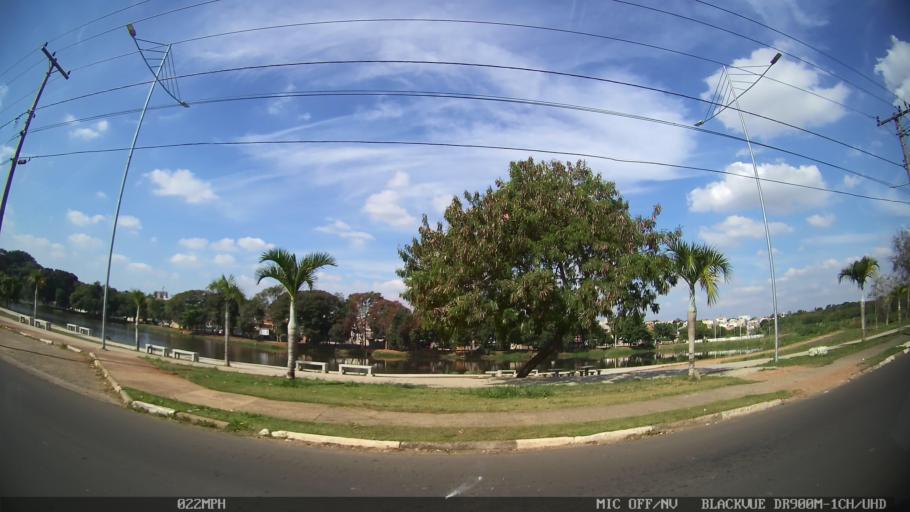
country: BR
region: Sao Paulo
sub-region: Hortolandia
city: Hortolandia
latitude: -22.8923
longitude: -47.2390
